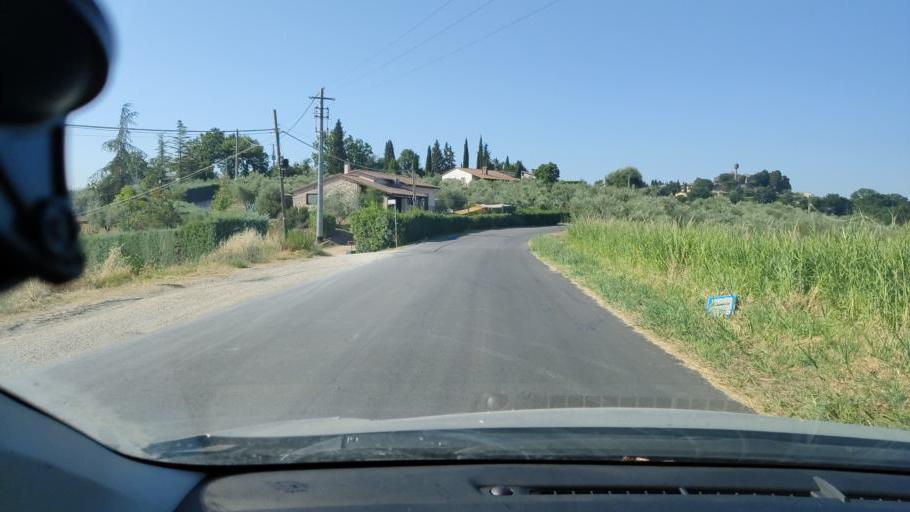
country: IT
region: Umbria
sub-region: Provincia di Terni
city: Fornole
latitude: 42.5204
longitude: 12.4328
